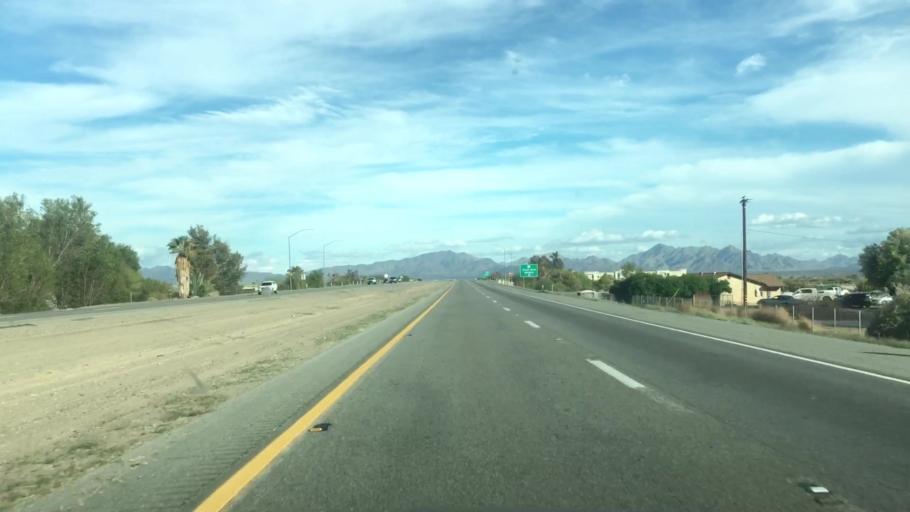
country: US
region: California
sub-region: Riverside County
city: Blythe
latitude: 33.6071
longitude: -114.5772
